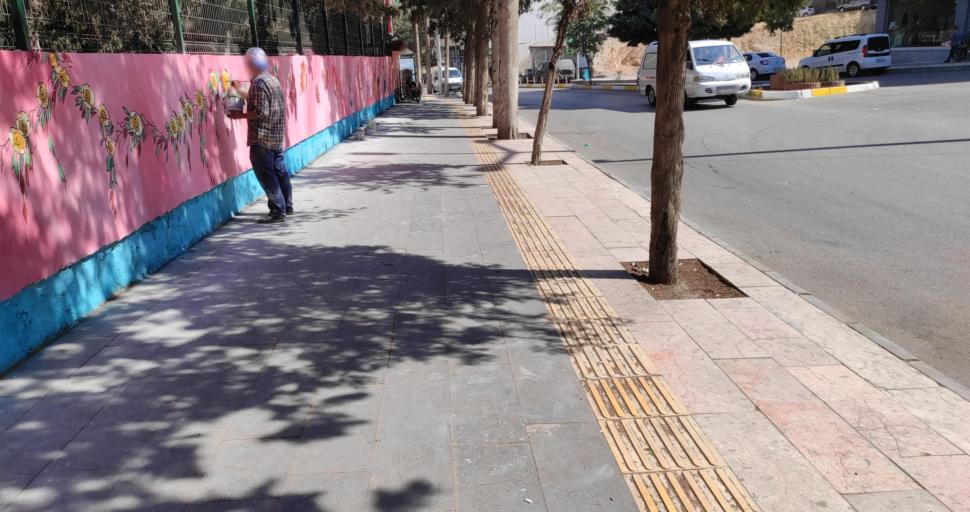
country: TR
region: Kilis
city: Kilis
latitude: 36.7224
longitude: 37.1061
